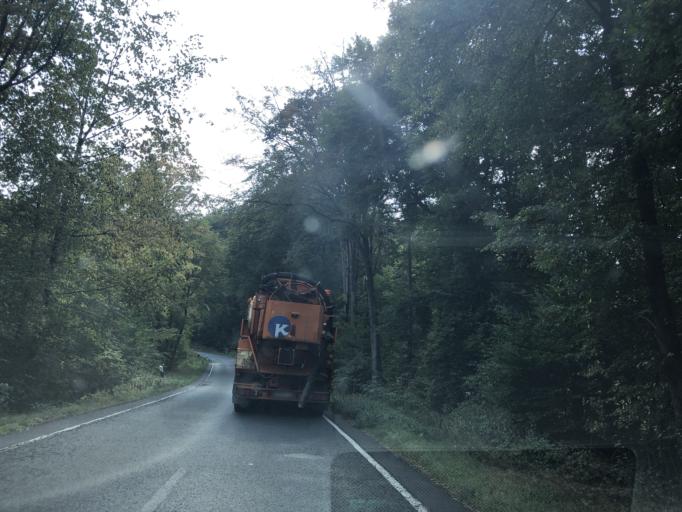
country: DE
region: Hesse
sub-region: Regierungsbezirk Giessen
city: Rauschenberg
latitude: 50.8776
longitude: 8.9507
